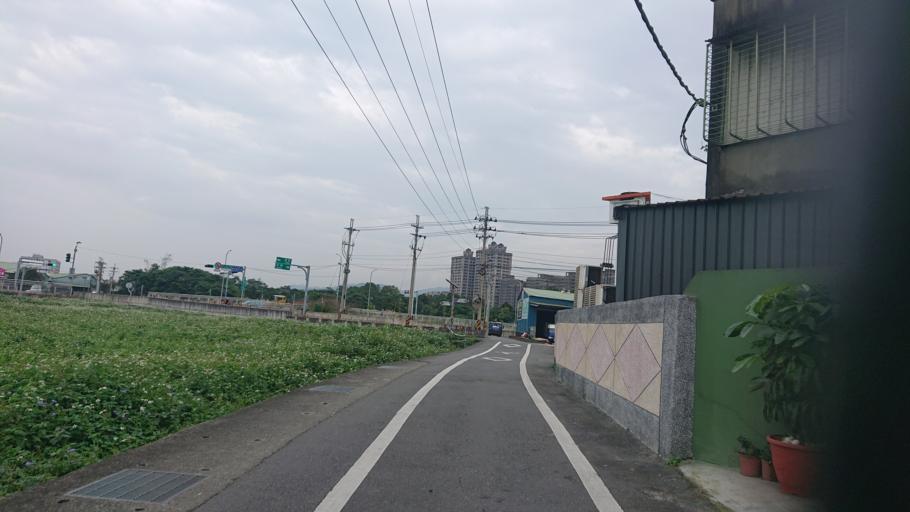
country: TW
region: Taiwan
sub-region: Taoyuan
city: Taoyuan
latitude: 24.9523
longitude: 121.3739
